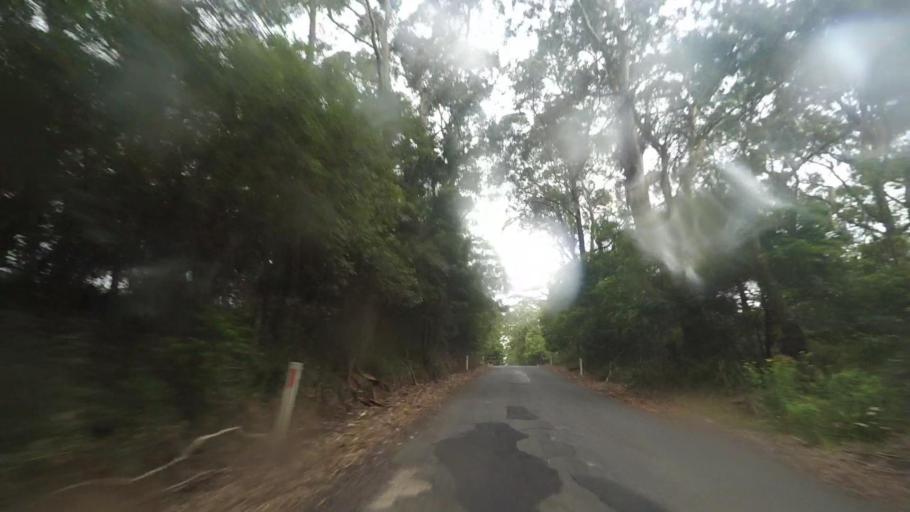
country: AU
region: New South Wales
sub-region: Wollongong
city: Mount Keira
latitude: -34.4019
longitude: 150.8326
